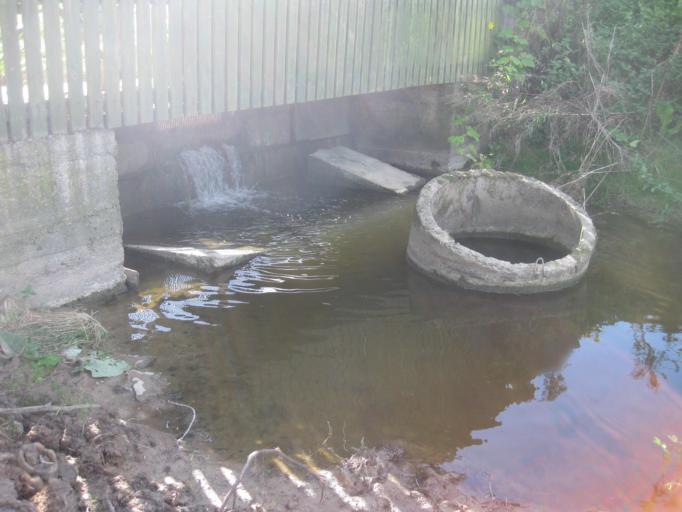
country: LT
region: Kauno apskritis
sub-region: Kauno rajonas
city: Garliava
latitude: 54.8310
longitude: 23.8717
